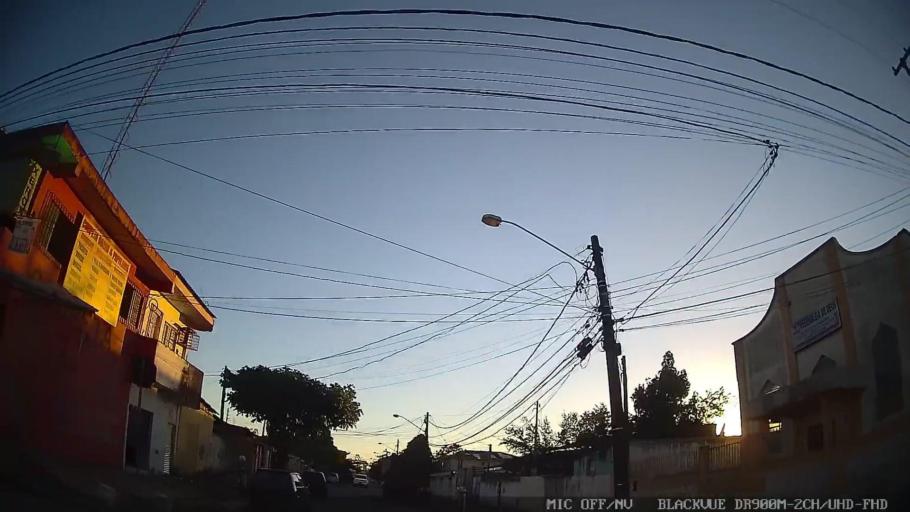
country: BR
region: Sao Paulo
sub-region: Guaruja
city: Guaruja
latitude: -23.9606
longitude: -46.2796
